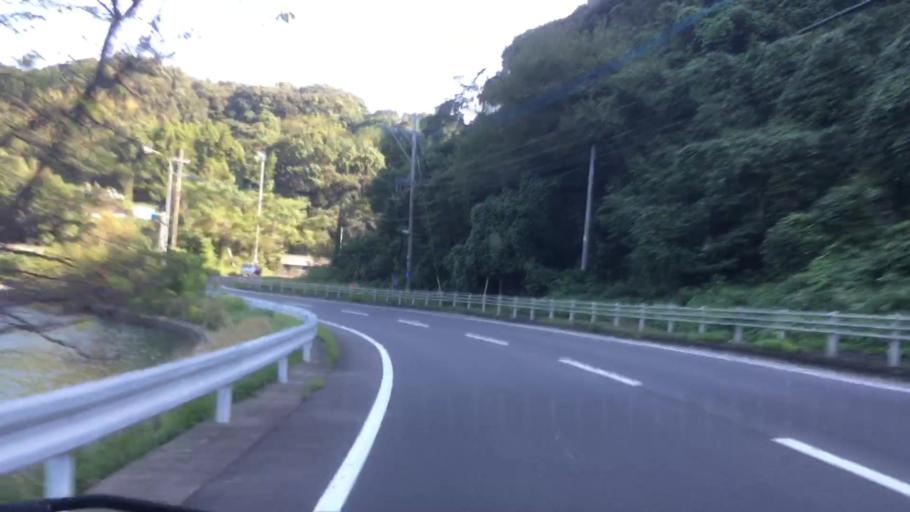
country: JP
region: Nagasaki
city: Sasebo
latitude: 32.9999
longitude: 129.6617
